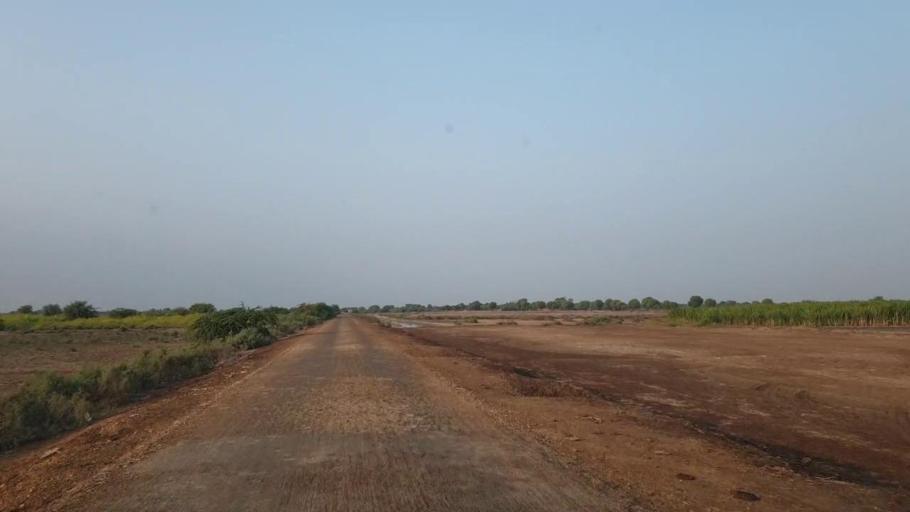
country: PK
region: Sindh
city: Tando Ghulam Ali
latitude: 25.0571
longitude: 68.9604
